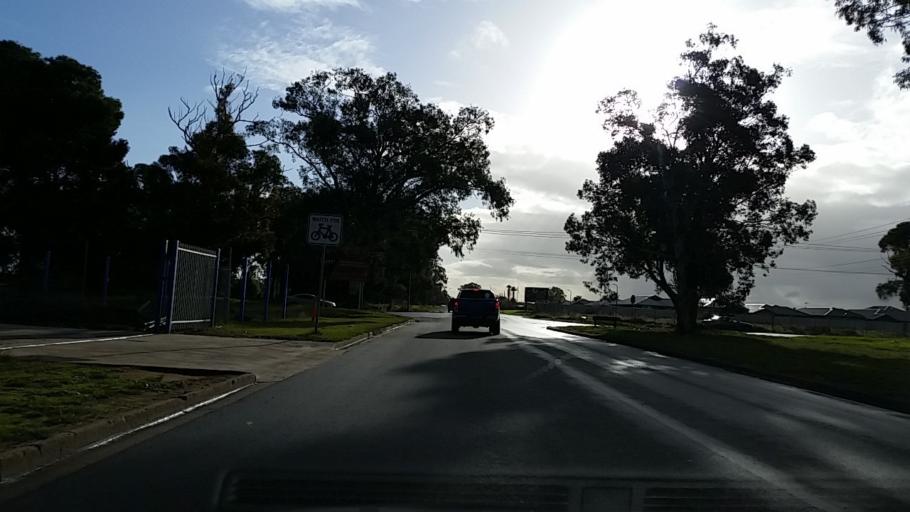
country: AU
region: South Australia
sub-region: Salisbury
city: Elizabeth
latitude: -34.6977
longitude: 138.6566
